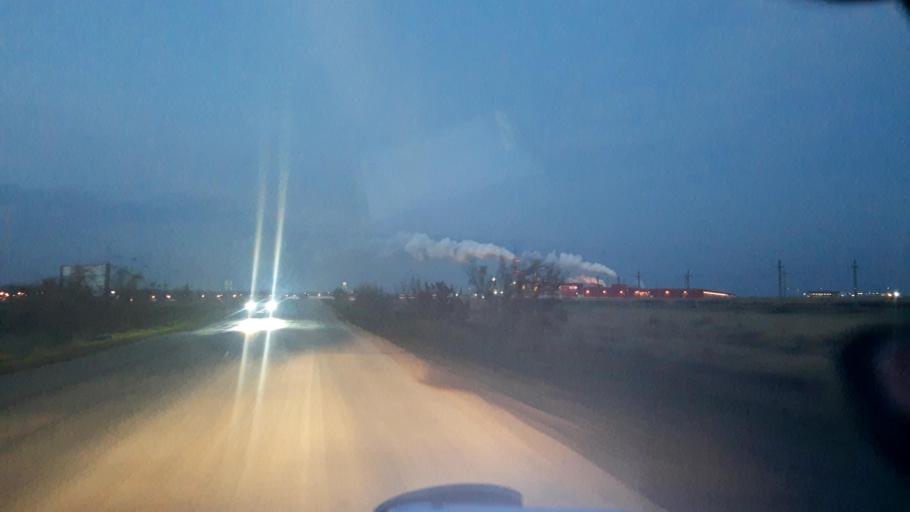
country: RU
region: Bashkortostan
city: Iglino
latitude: 54.7590
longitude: 56.2592
